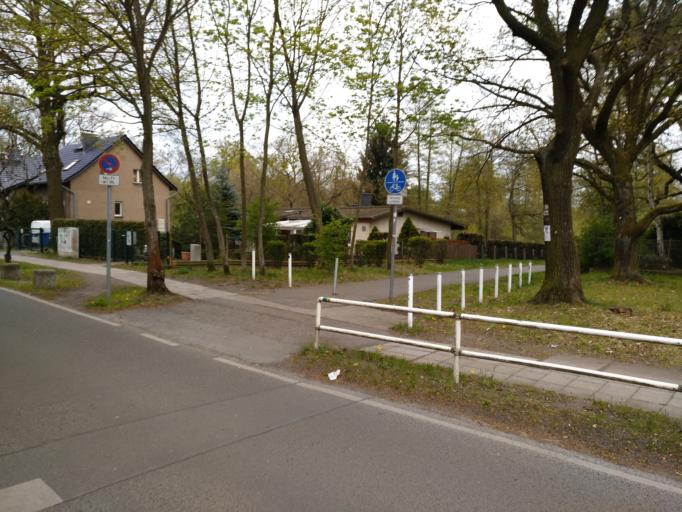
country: DE
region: Berlin
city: Berlin Koepenick
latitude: 52.4576
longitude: 13.6012
